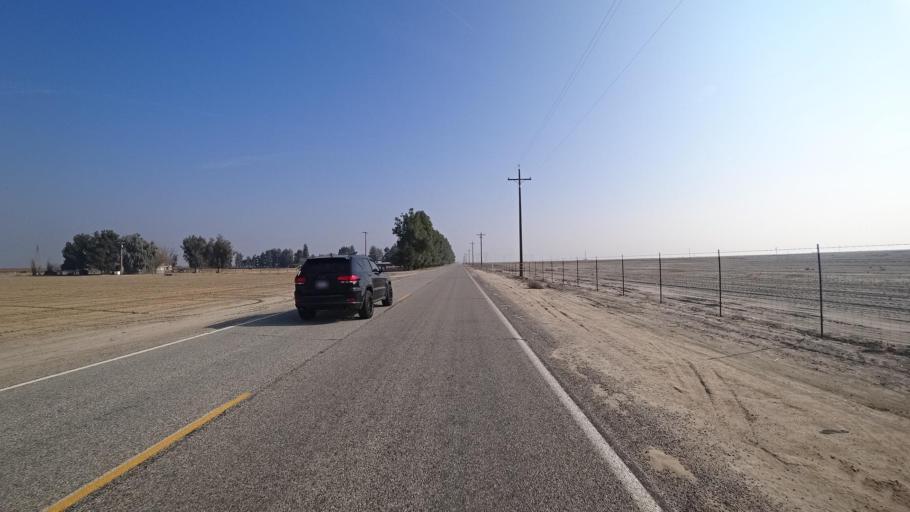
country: US
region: California
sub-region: Kern County
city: Buttonwillow
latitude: 35.3548
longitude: -119.3721
